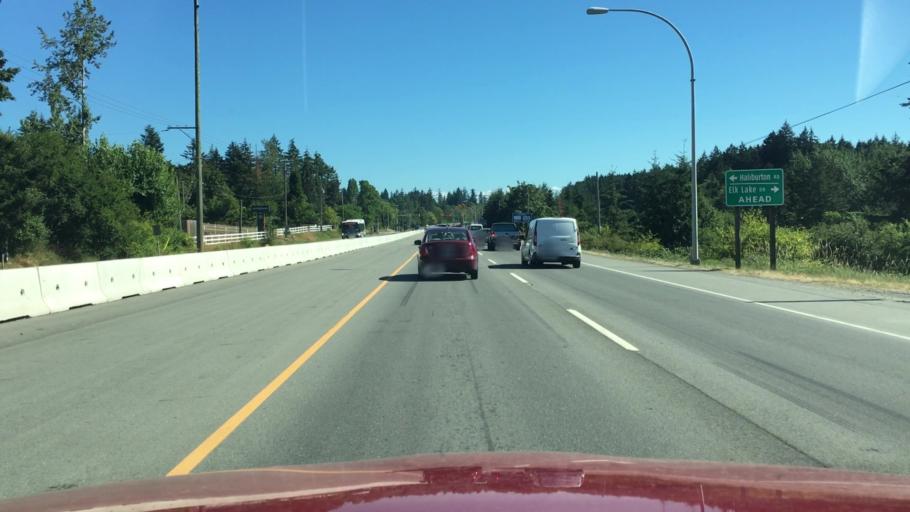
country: CA
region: British Columbia
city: Victoria
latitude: 48.5176
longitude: -123.3851
